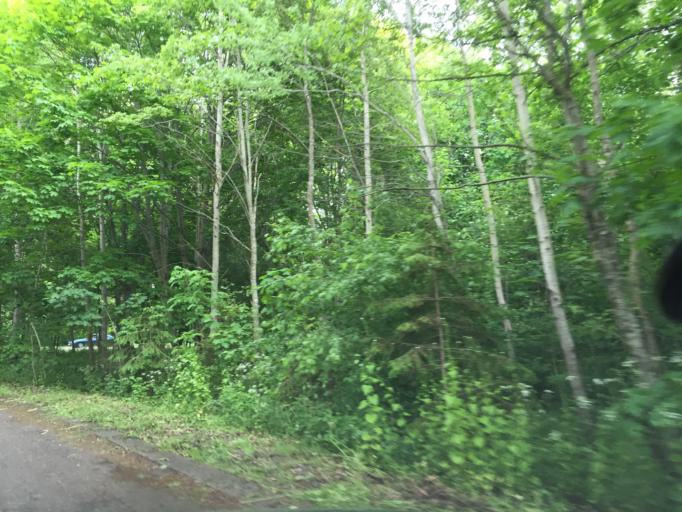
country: LT
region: Klaipedos apskritis
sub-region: Klaipeda
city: Klaipeda
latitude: 55.7617
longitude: 21.0879
